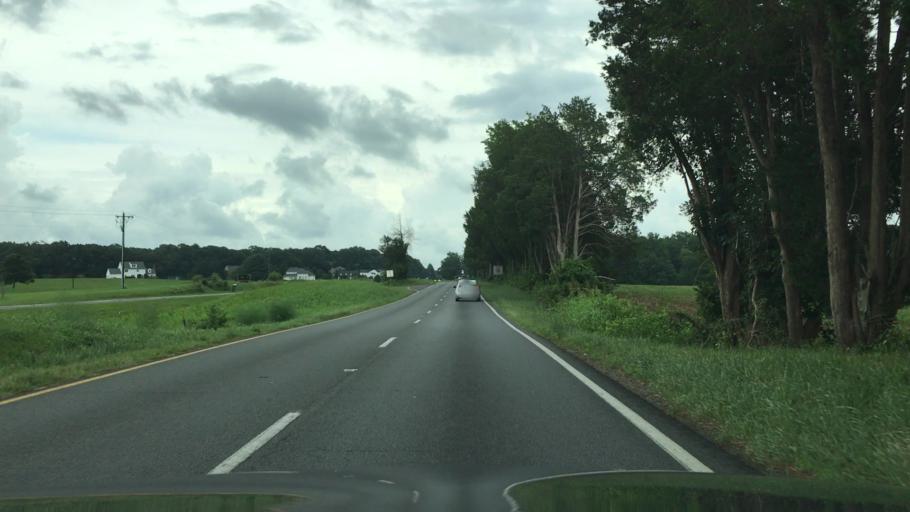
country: US
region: Virginia
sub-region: Spotsylvania County
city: Spotsylvania
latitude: 38.3245
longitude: -77.7211
